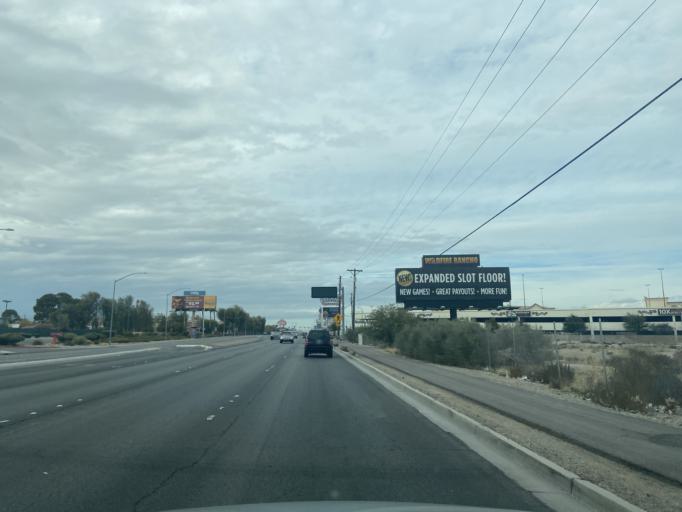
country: US
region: Nevada
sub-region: Clark County
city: Las Vegas
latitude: 36.1944
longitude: -115.1912
